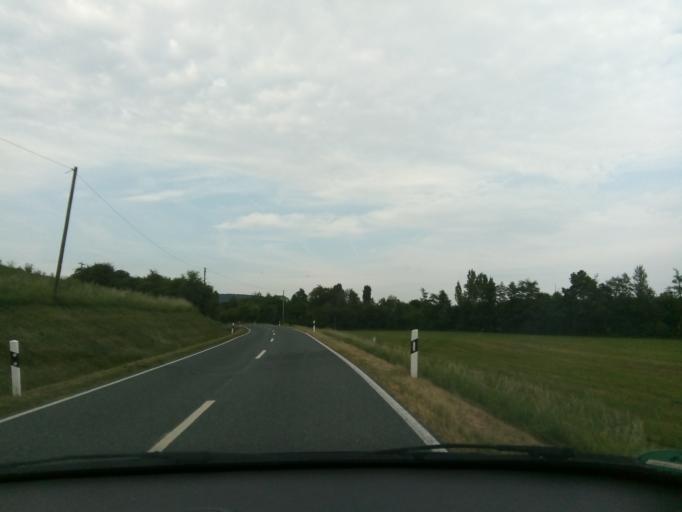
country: DE
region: Bavaria
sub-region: Regierungsbezirk Unterfranken
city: Oberschwarzach
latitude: 49.8573
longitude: 10.3958
